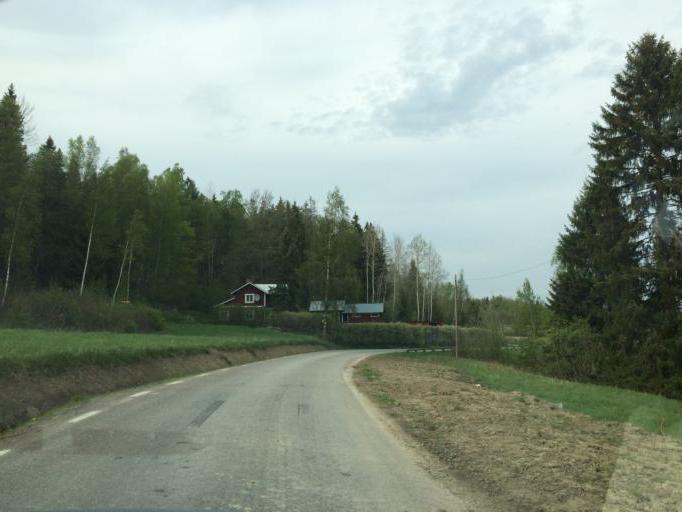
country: SE
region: Vaestmanland
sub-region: Kopings Kommun
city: Koping
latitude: 59.5874
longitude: 15.9869
